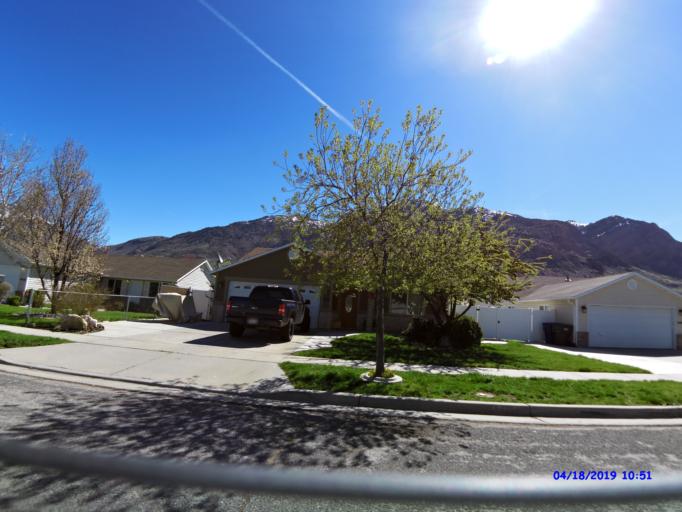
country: US
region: Utah
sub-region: Weber County
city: North Ogden
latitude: 41.2843
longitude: -111.9611
